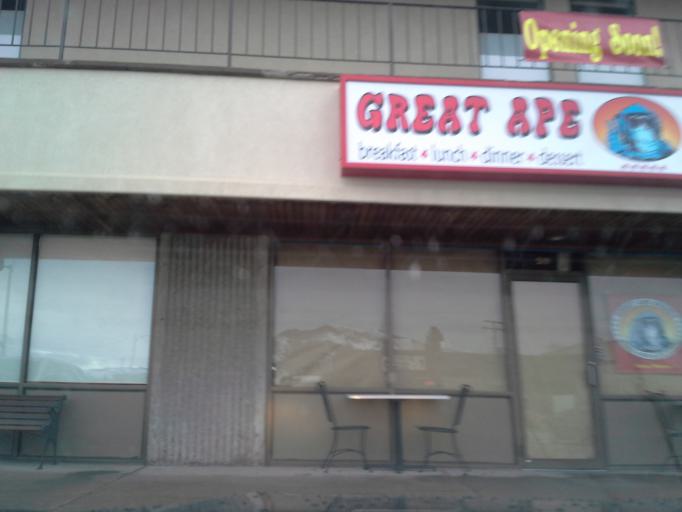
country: US
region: Montana
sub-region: Lewis and Clark County
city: Helena
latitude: 46.5895
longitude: -112.0145
